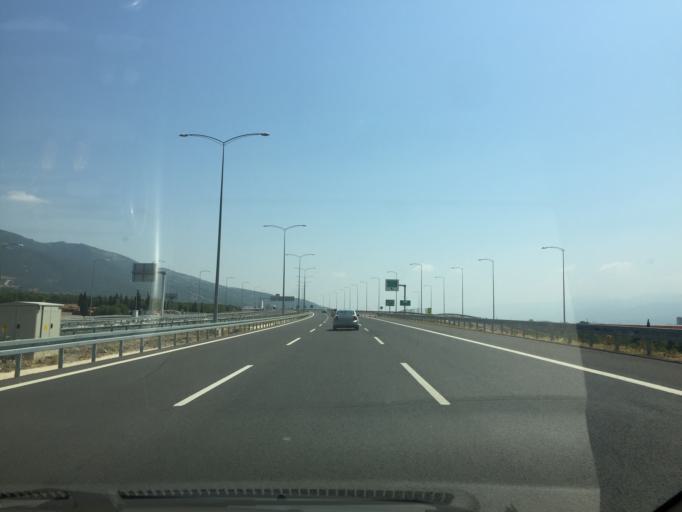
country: TR
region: Izmir
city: Kemalpasa
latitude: 38.4624
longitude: 27.4342
